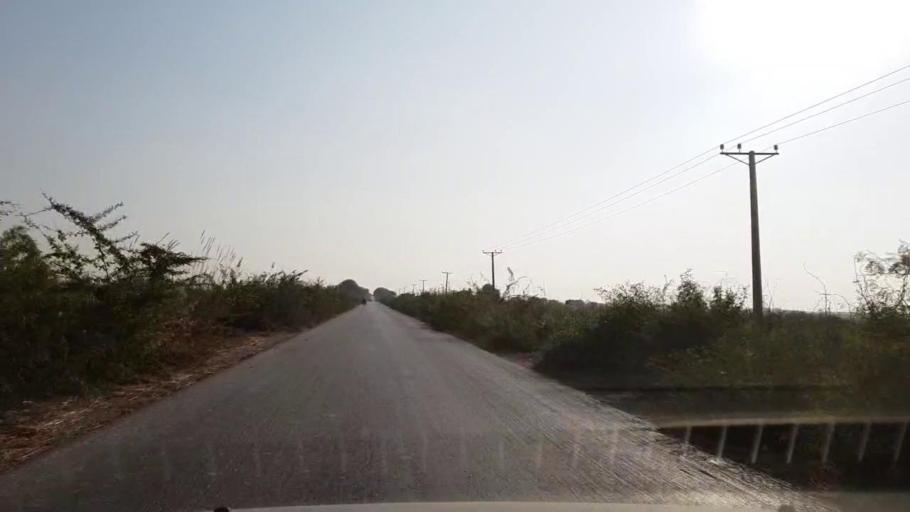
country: PK
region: Sindh
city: Bulri
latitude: 24.8807
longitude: 68.3414
